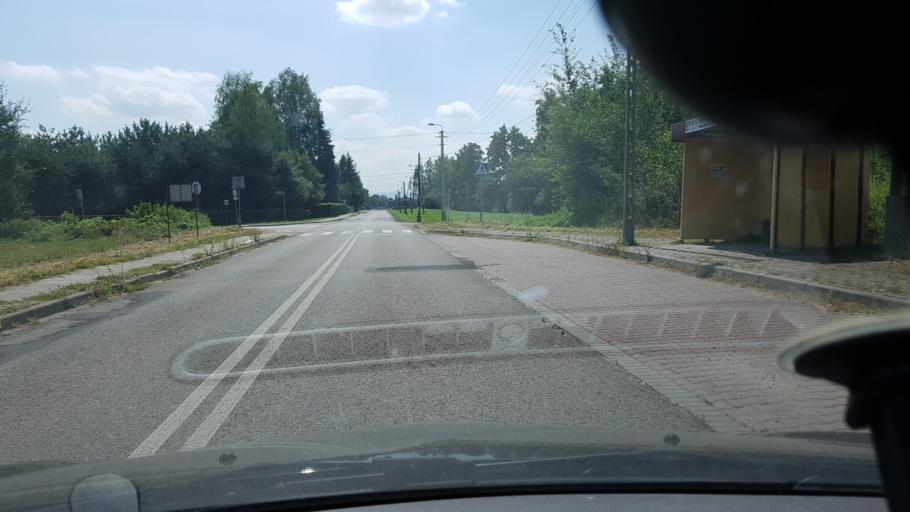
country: PL
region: Lesser Poland Voivodeship
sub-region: Powiat oswiecimski
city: Brzezinka
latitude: 50.0434
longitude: 19.1814
